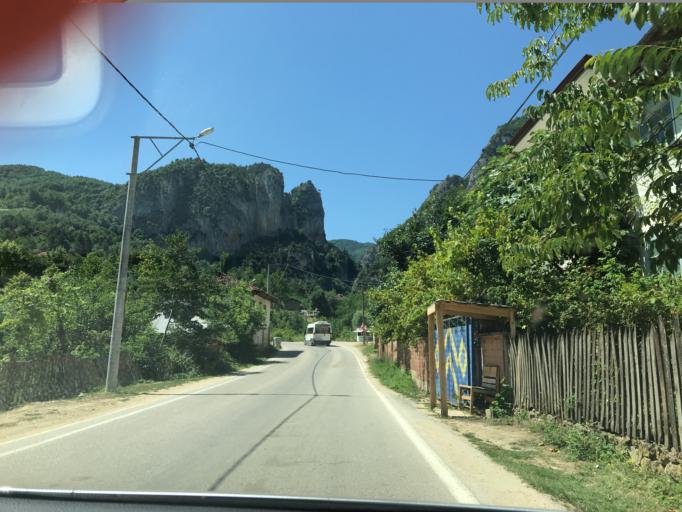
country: TR
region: Bursa
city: Tahtakopru
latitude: 39.9495
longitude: 29.5944
